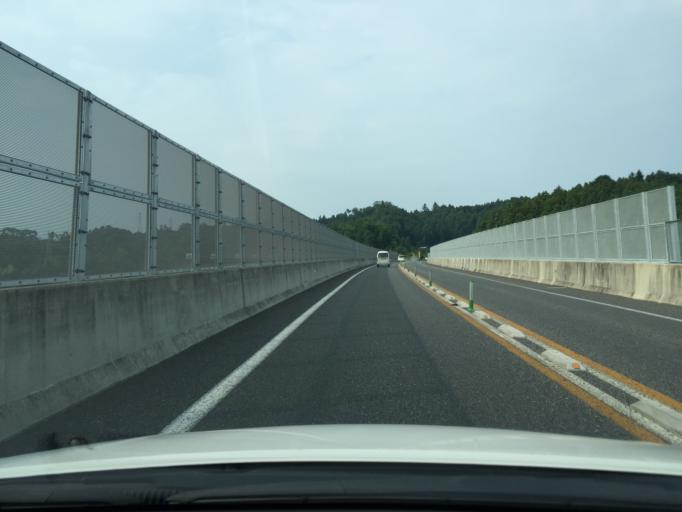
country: JP
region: Fukushima
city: Iwaki
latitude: 37.1690
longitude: 140.9680
